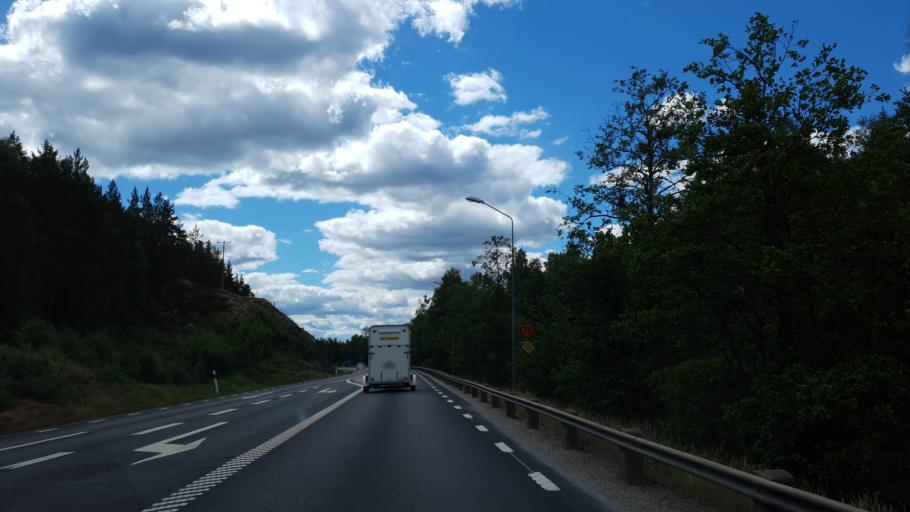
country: SE
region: Kronoberg
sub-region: Vaxjo Kommun
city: Braas
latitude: 57.2195
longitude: 15.1457
